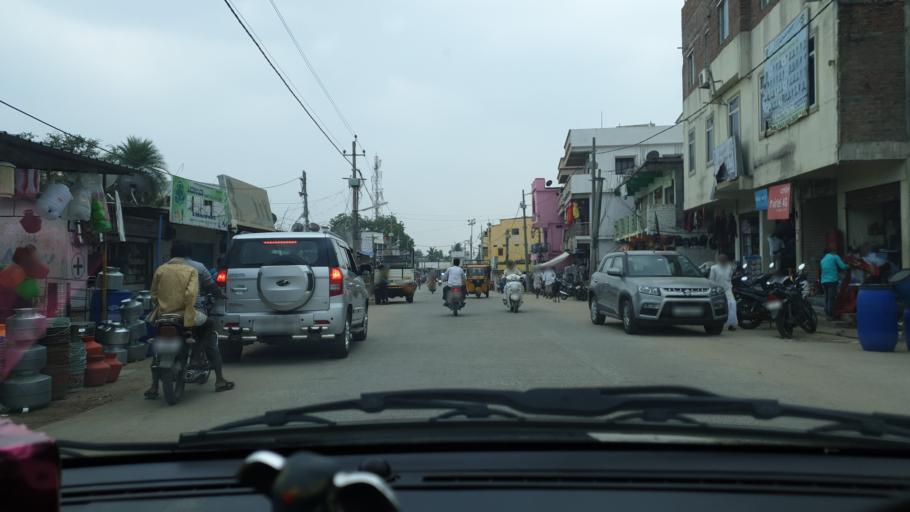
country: IN
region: Karnataka
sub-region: Yadgir
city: Gurmatkal
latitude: 16.8685
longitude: 77.3916
